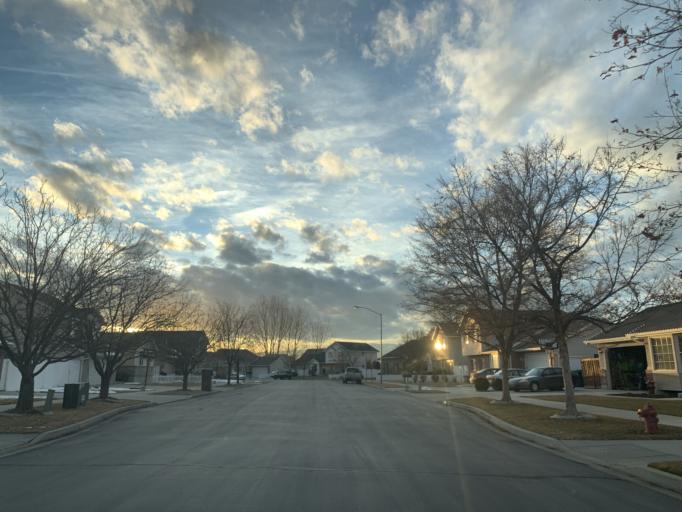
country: US
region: Utah
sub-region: Utah County
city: Provo
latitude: 40.2411
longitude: -111.7079
